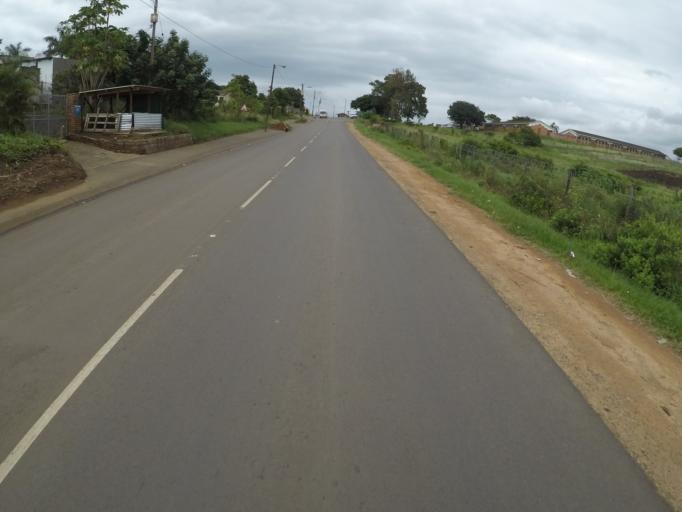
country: ZA
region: KwaZulu-Natal
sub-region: uThungulu District Municipality
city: Empangeni
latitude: -28.7829
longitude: 31.8577
